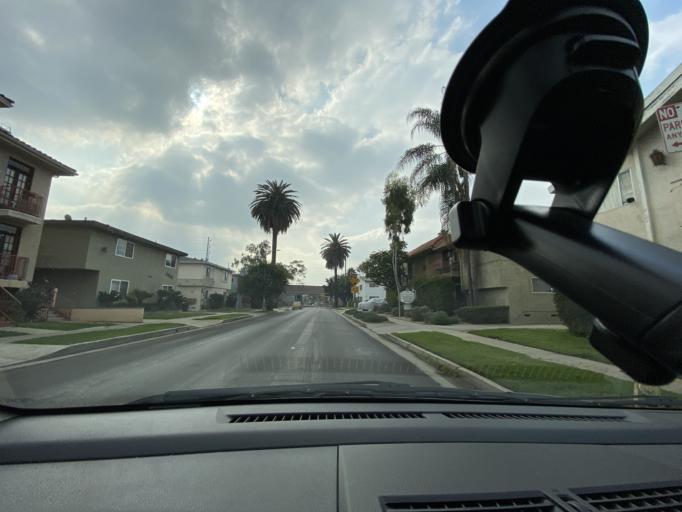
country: US
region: California
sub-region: Los Angeles County
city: Culver City
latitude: 34.0304
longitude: -118.3964
